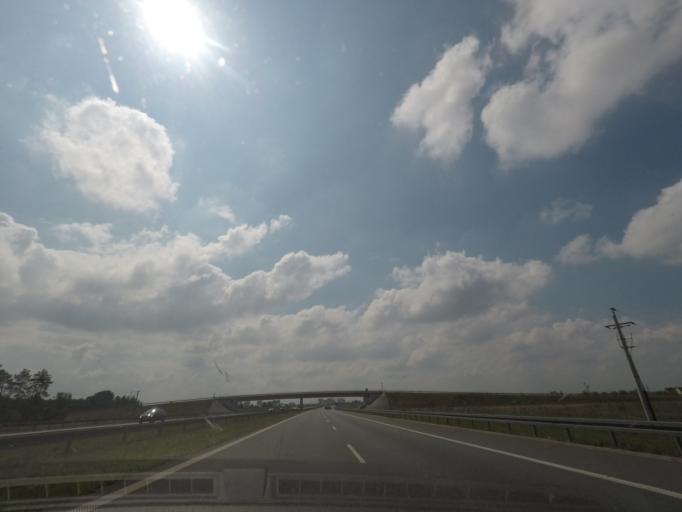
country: PL
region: Lodz Voivodeship
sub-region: Powiat kutnowski
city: Krzyzanow
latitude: 52.1939
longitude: 19.4872
